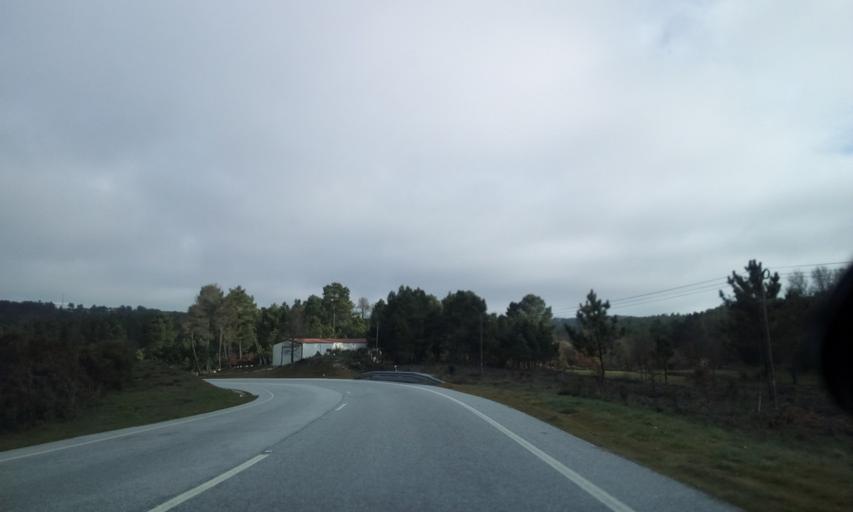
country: PT
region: Guarda
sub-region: Aguiar da Beira
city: Aguiar da Beira
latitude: 40.7771
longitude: -7.5051
